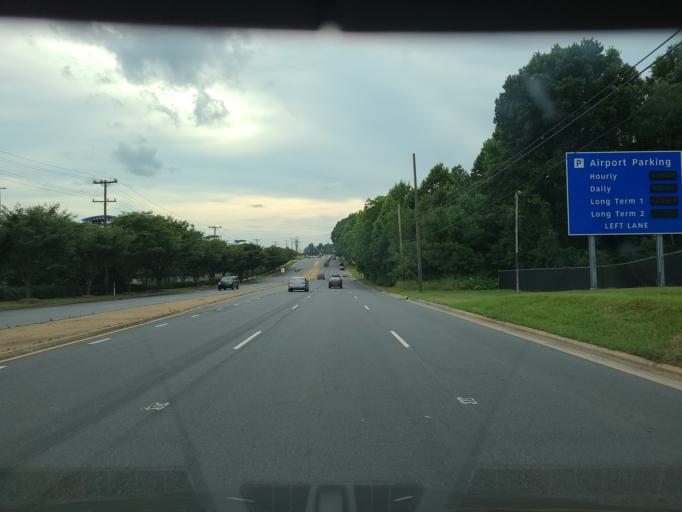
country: US
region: North Carolina
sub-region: Mecklenburg County
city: Charlotte
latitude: 35.2342
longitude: -80.9349
